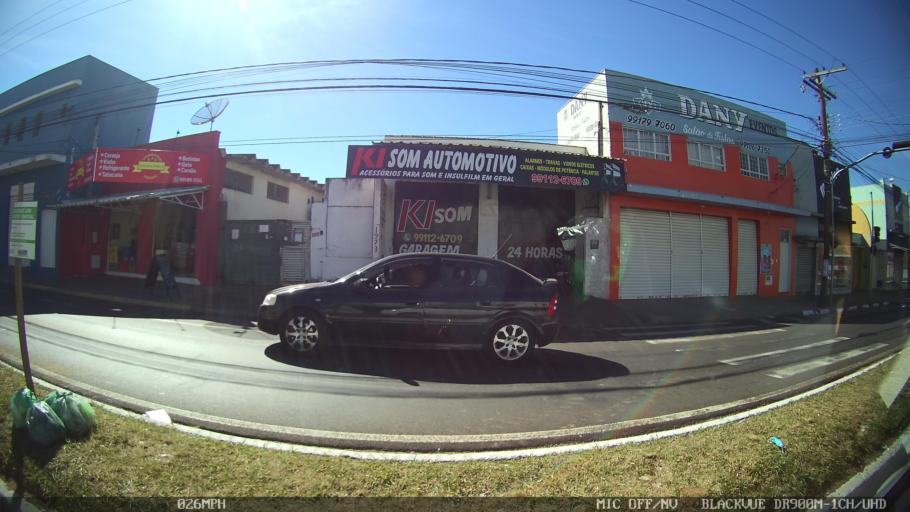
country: BR
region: Sao Paulo
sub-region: Franca
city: Franca
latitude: -20.5329
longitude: -47.3660
